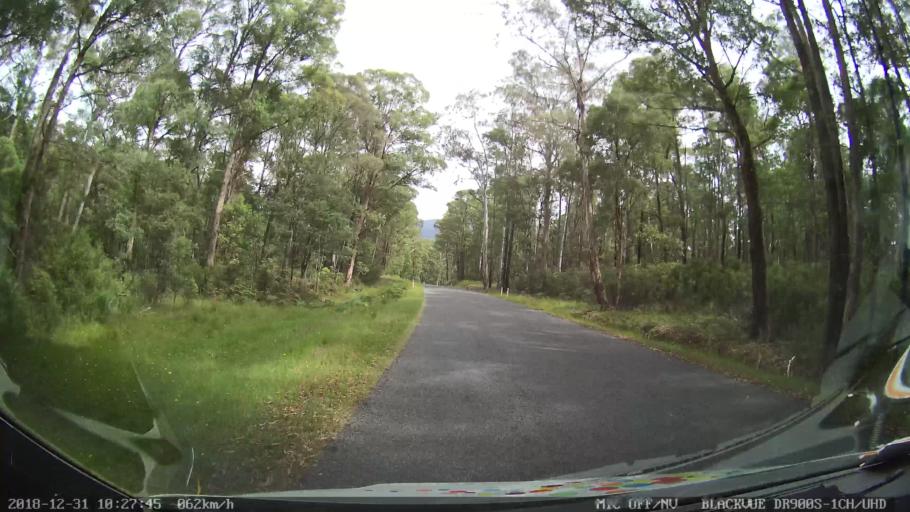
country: AU
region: New South Wales
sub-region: Snowy River
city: Jindabyne
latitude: -36.4841
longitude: 148.1447
